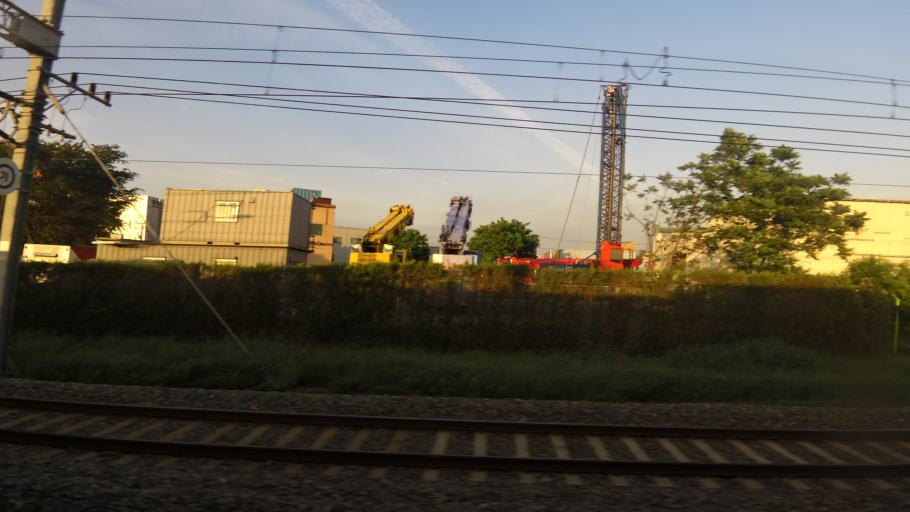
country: KR
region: Gyeonggi-do
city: Osan
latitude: 37.0293
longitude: 127.0693
